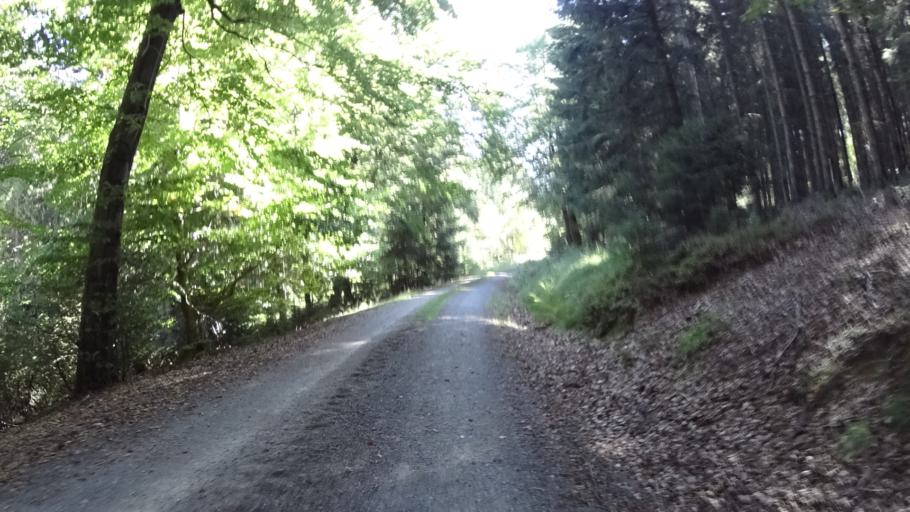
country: DE
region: Thuringia
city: Langewiesen
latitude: 50.6332
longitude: 10.9538
